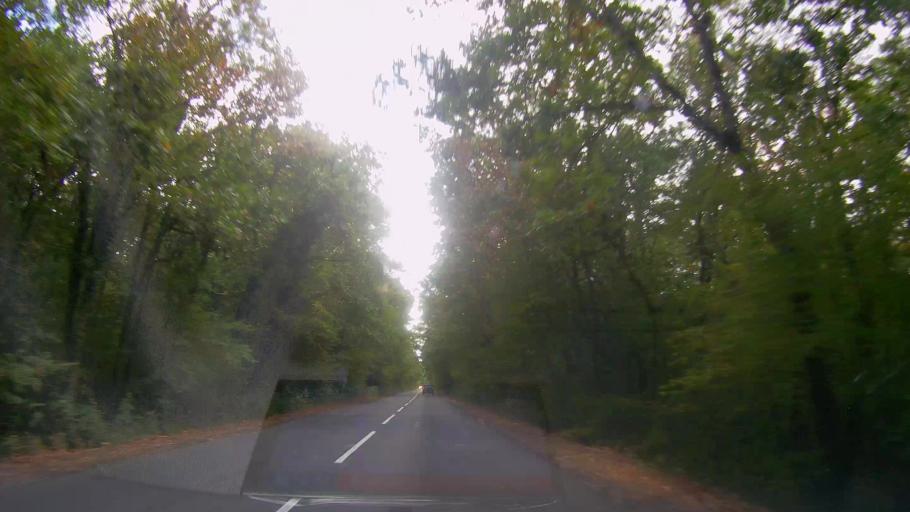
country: BG
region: Burgas
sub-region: Obshtina Primorsko
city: Primorsko
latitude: 42.2982
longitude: 27.7296
